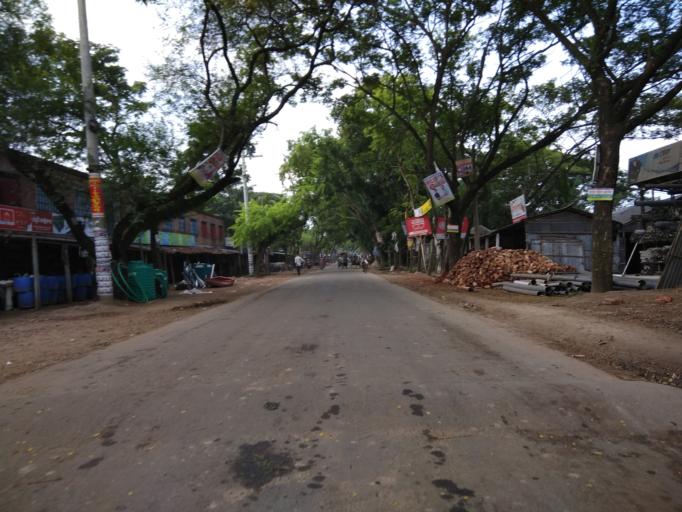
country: IN
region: West Bengal
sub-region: North 24 Parganas
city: Taki
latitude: 22.3390
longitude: 89.1060
